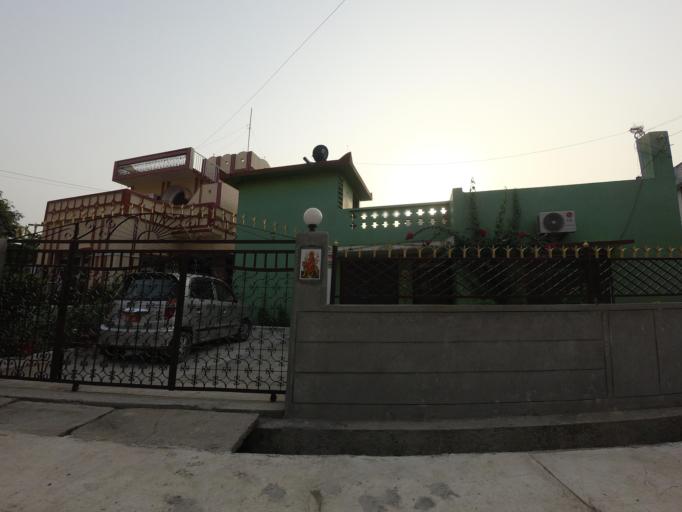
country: NP
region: Western Region
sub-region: Lumbini Zone
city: Bhairahawa
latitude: 27.5150
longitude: 83.4557
